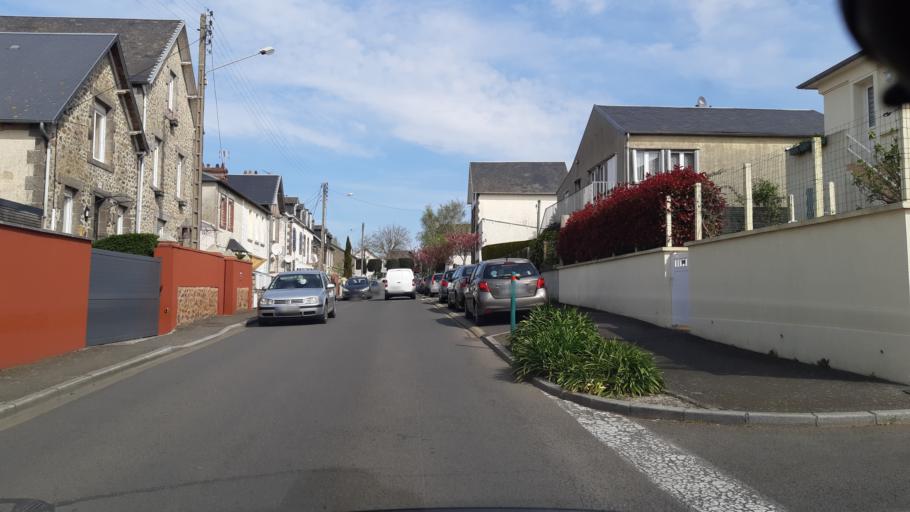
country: FR
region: Lower Normandy
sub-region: Departement de la Manche
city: Donville-les-Bains
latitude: 48.8466
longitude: -1.5780
